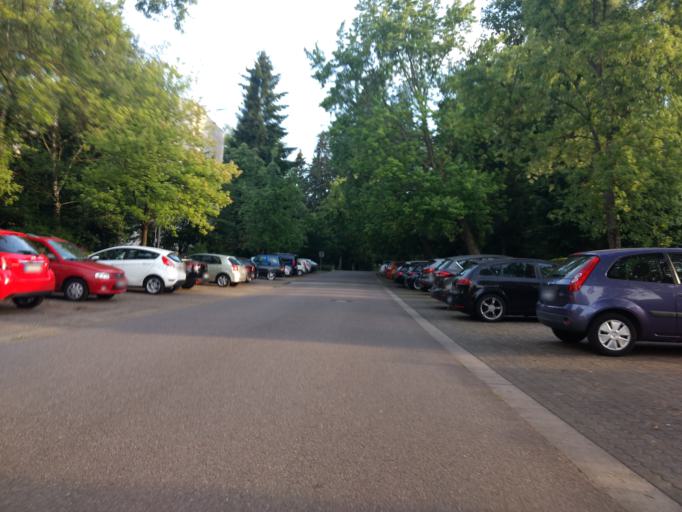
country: DE
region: Saarland
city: Saarlouis
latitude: 49.3044
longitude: 6.7357
